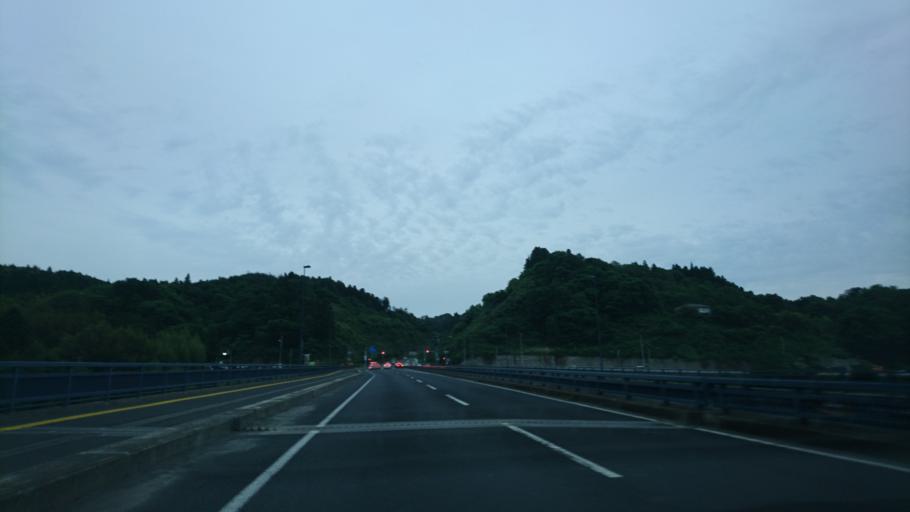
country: JP
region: Iwate
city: Ichinoseki
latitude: 38.9349
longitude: 141.1622
